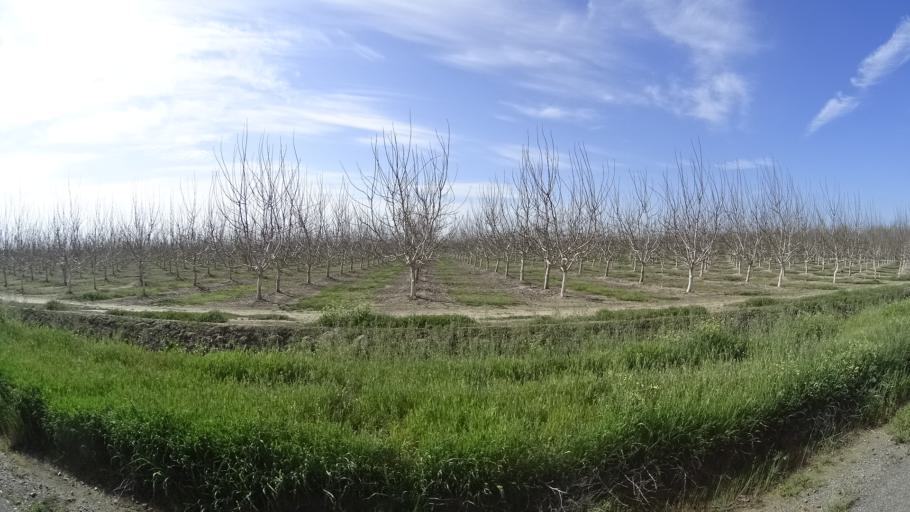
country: US
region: California
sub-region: Glenn County
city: Hamilton City
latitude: 39.6234
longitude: -122.0215
